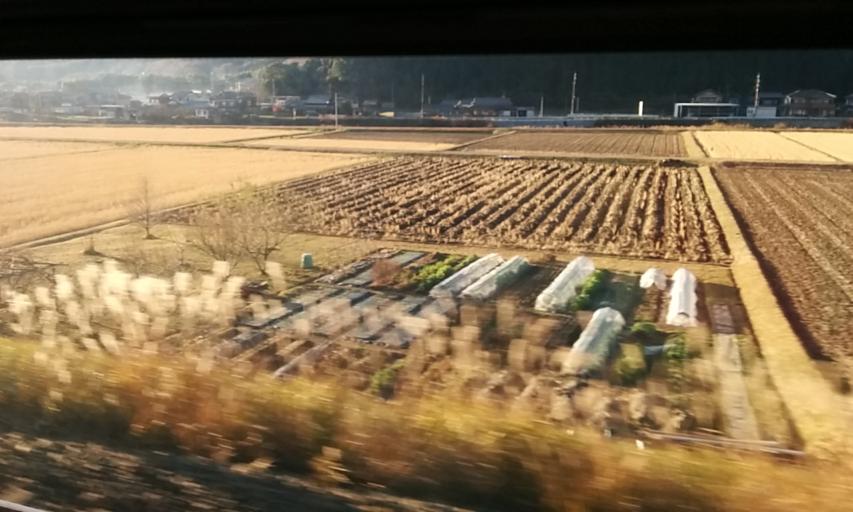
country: JP
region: Gifu
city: Mizunami
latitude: 35.4023
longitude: 137.2974
